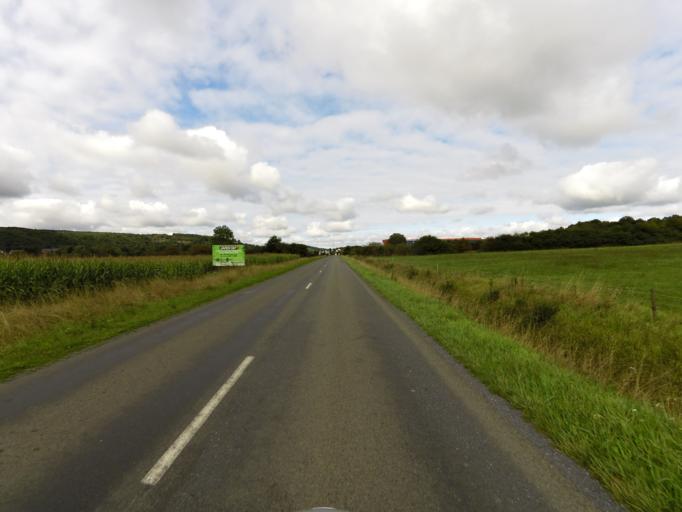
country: FR
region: Champagne-Ardenne
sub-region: Departement des Ardennes
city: Fromelennes
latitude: 50.1327
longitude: 4.8596
